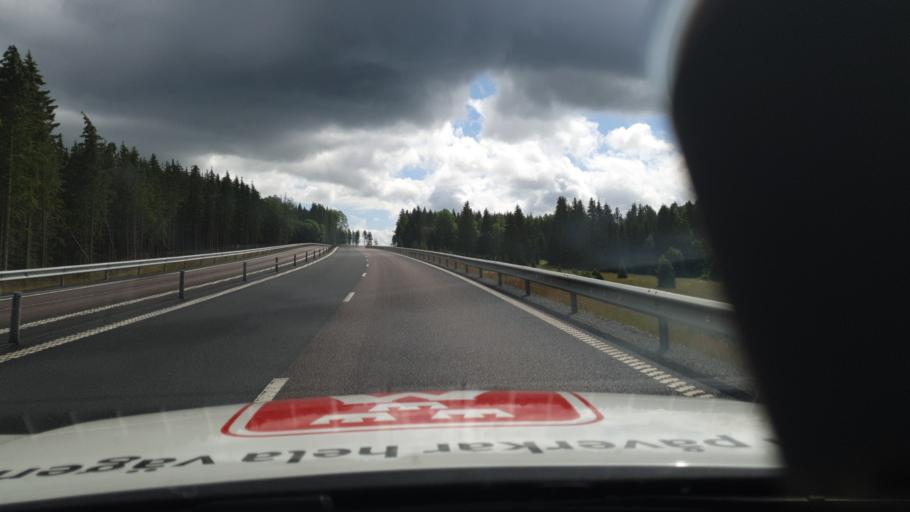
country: SE
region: Joenkoeping
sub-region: Mullsjo Kommun
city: Mullsjoe
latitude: 57.8964
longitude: 13.8724
